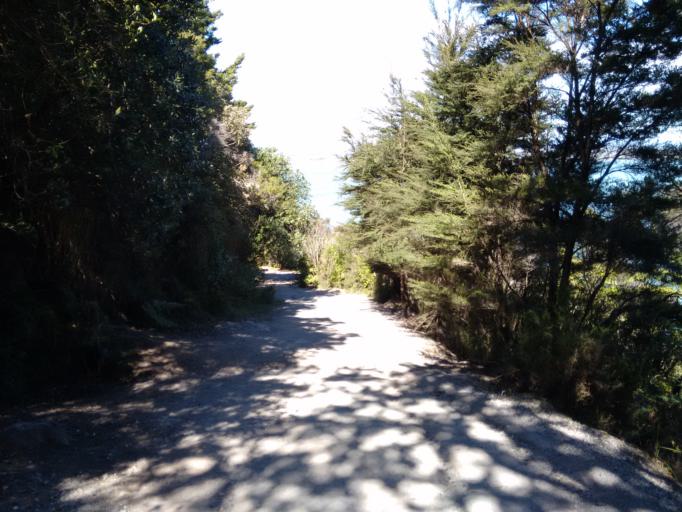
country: NZ
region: Bay of Plenty
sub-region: Tauranga City
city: Tauranga
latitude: -37.6303
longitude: 176.1687
